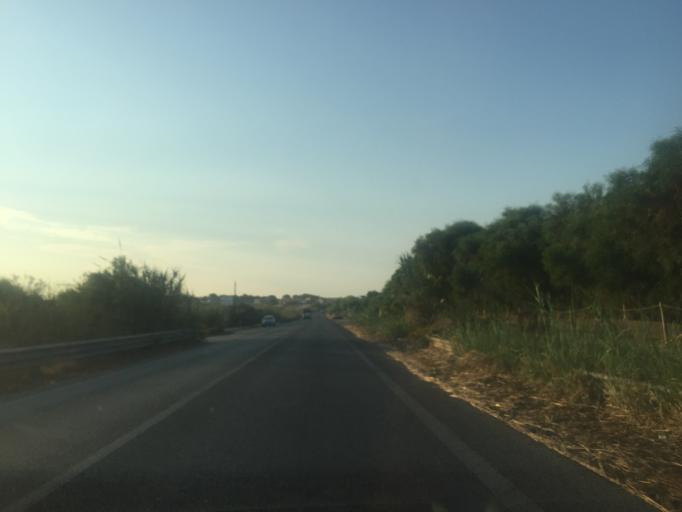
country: IT
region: Sicily
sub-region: Ragusa
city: Cava d'Aliga
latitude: 36.7200
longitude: 14.7537
